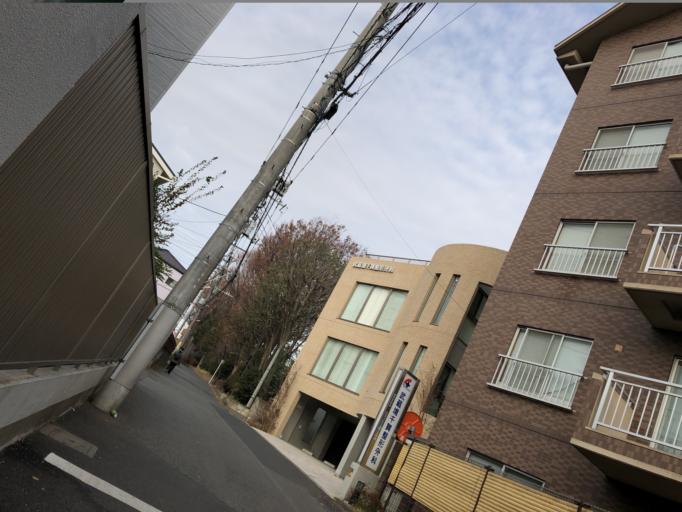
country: JP
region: Tokyo
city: Kamirenjaku
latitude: 35.6959
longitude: 139.5455
